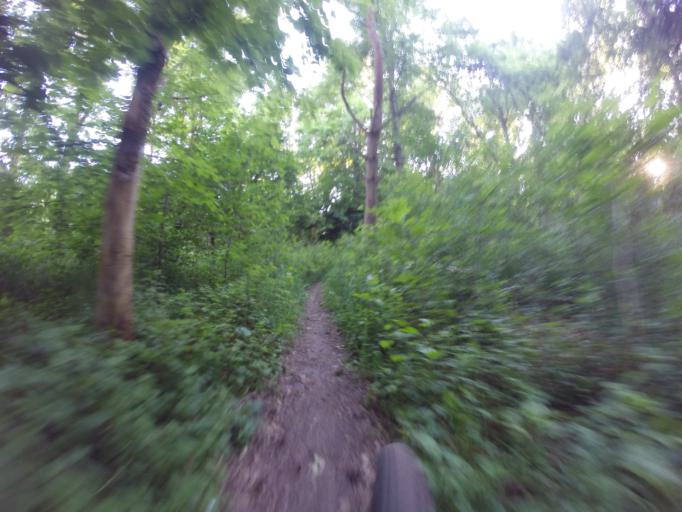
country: DK
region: Capital Region
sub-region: Hoje-Taastrup Kommune
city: Taastrup
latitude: 55.6830
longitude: 12.3162
